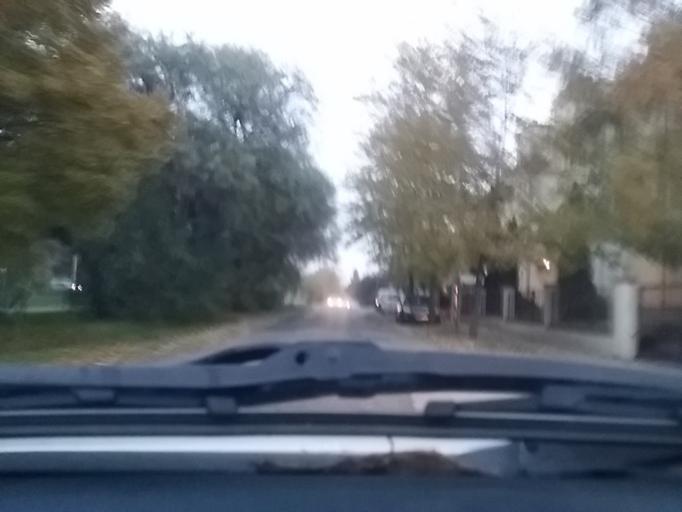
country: HU
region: Budapest
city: Budapest XIV. keruelet
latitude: 47.5185
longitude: 19.1385
